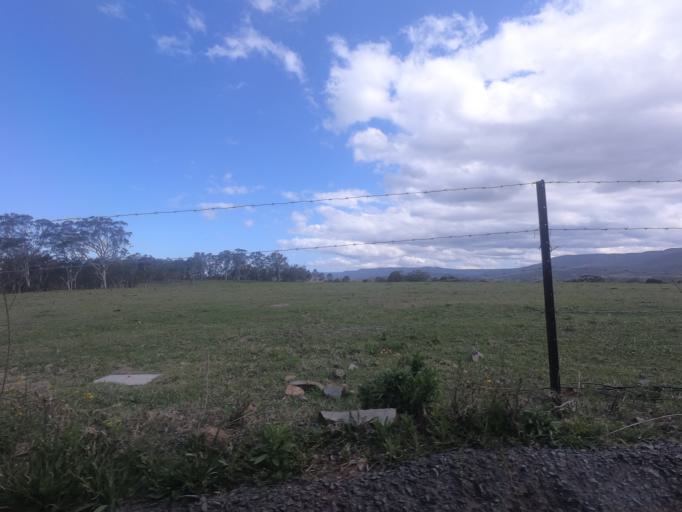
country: AU
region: New South Wales
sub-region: Wollongong
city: Dapto
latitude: -34.4710
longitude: 150.7761
